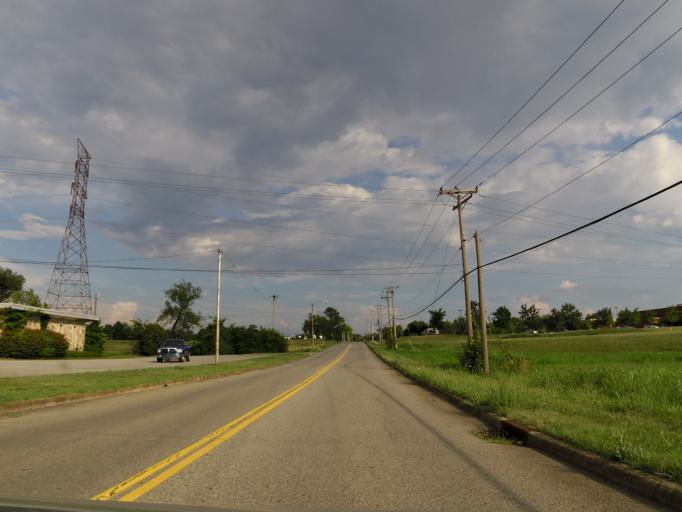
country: US
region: Tennessee
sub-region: Blount County
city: Maryville
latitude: 35.7699
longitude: -83.9780
